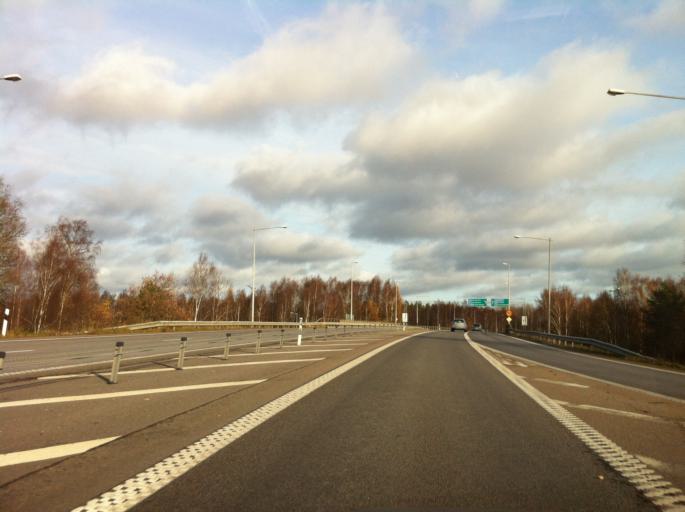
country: SE
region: Kronoberg
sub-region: Vaxjo Kommun
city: Gemla
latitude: 56.8130
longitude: 14.6755
